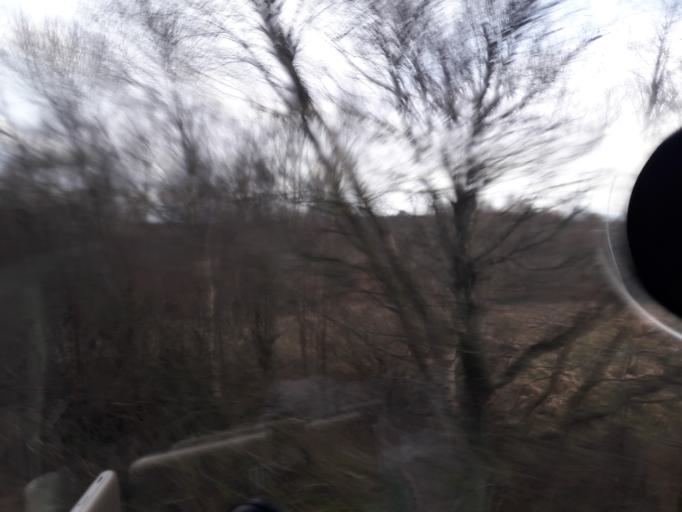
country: IE
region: Leinster
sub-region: An Iarmhi
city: Kinnegad
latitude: 53.4845
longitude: -7.0992
